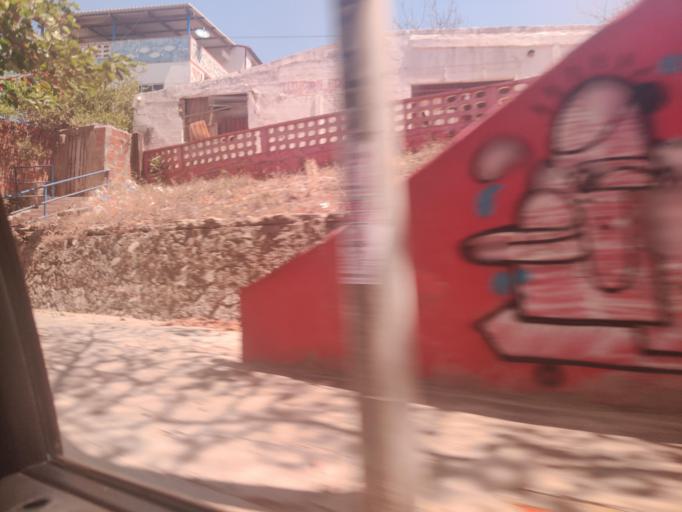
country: CO
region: Atlantico
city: Puerto Colombia
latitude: 10.9980
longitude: -74.9522
